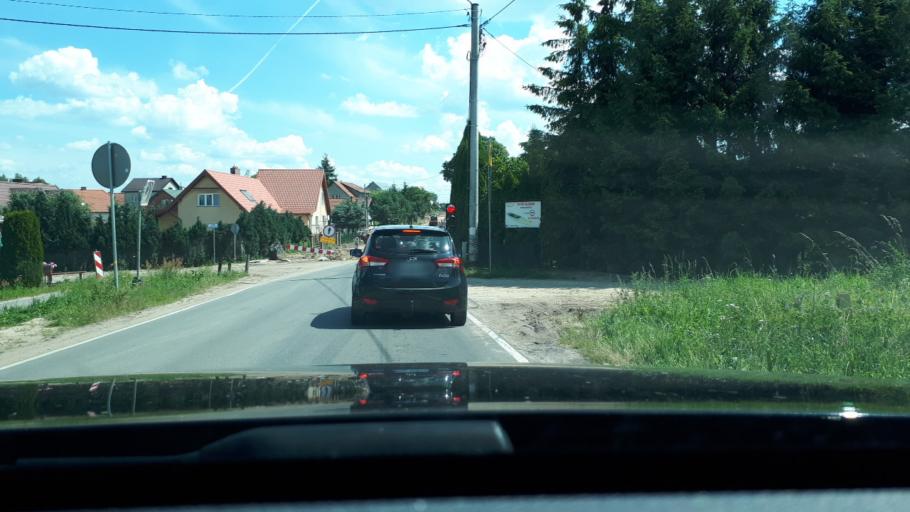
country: PL
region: Warmian-Masurian Voivodeship
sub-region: Powiat olsztynski
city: Olsztynek
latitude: 53.5852
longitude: 20.3174
